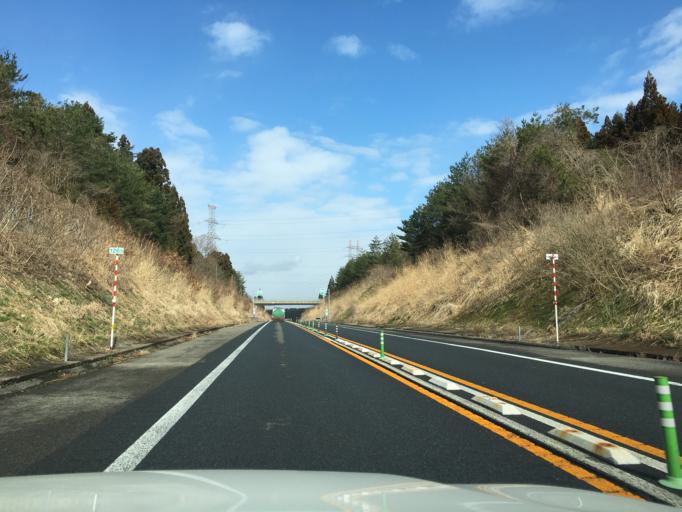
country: JP
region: Akita
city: Akita Shi
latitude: 39.8096
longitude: 140.0935
